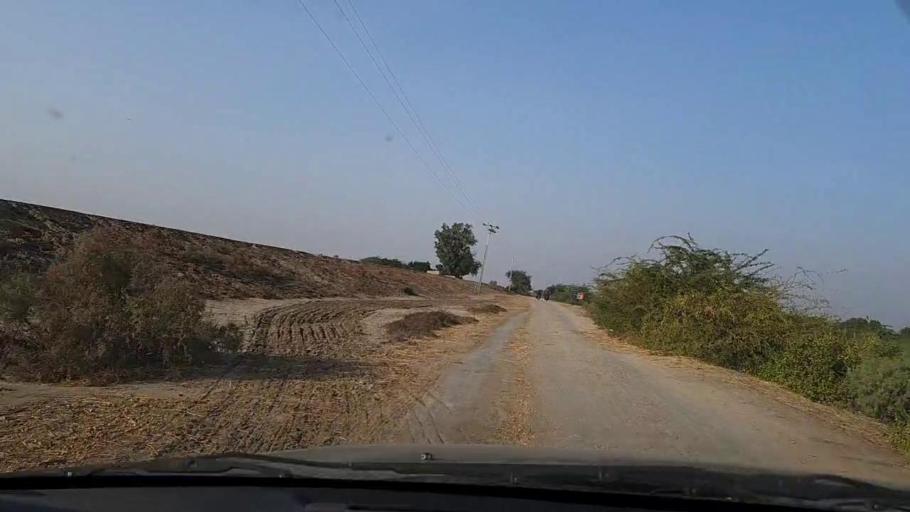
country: PK
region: Sindh
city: Chuhar Jamali
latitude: 24.2936
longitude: 67.7550
